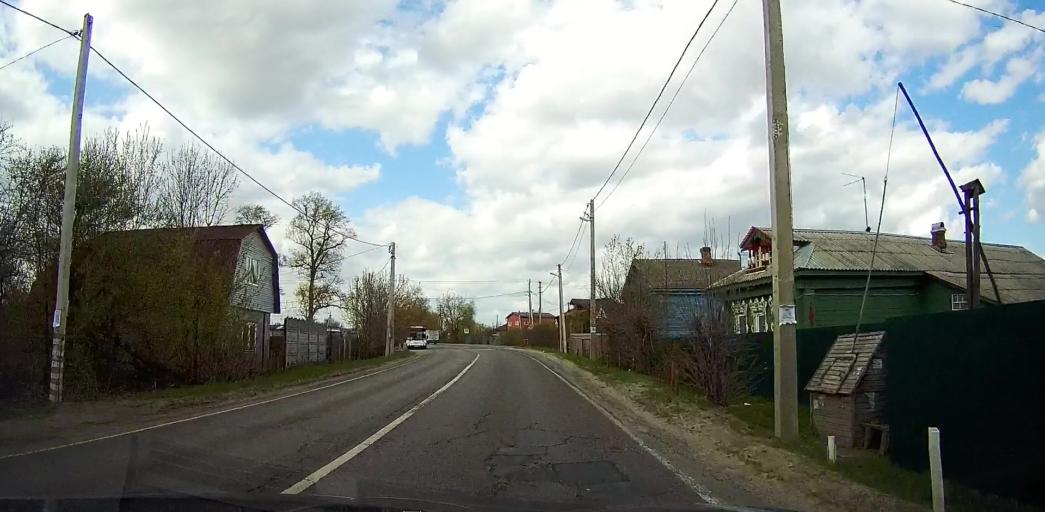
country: RU
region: Moskovskaya
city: Davydovo
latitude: 55.6358
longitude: 38.8688
